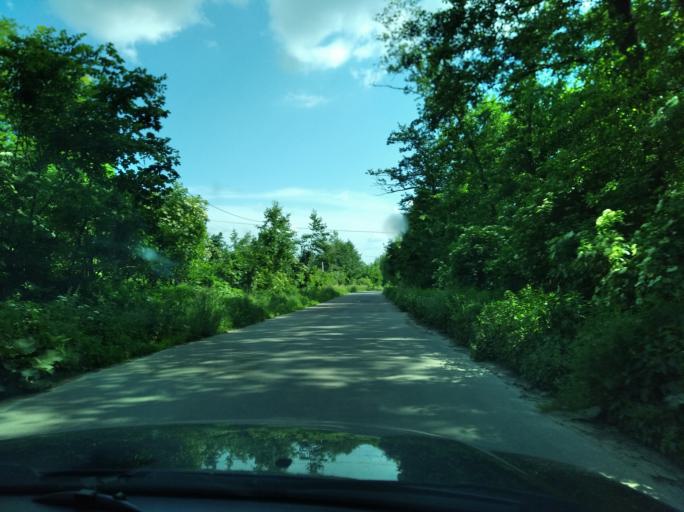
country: PL
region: Subcarpathian Voivodeship
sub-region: Powiat jaroslawski
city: Ostrow
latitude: 49.9393
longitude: 22.7396
